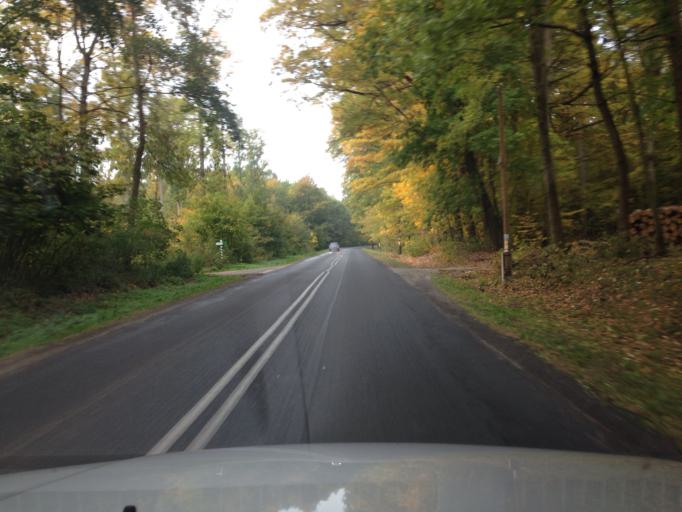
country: PL
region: Kujawsko-Pomorskie
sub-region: Powiat brodnicki
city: Bobrowo
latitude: 53.2670
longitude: 19.3234
